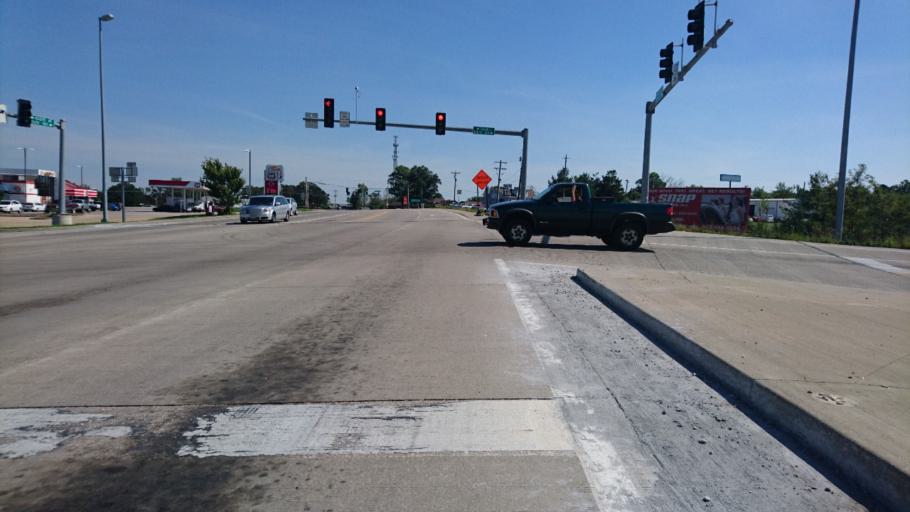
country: US
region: Missouri
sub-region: Franklin County
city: Sullivan
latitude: 38.2237
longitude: -91.1543
